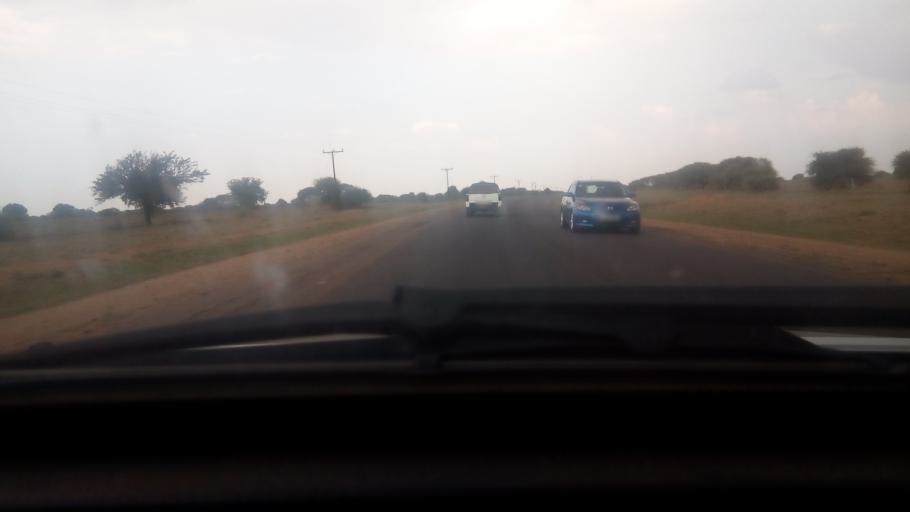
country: BW
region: Kweneng
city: Metsemotlhaba
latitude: -24.4789
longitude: 25.7290
